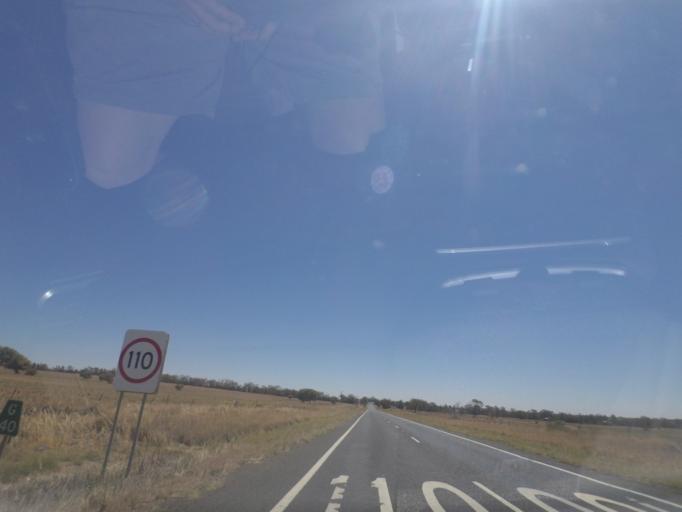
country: AU
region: New South Wales
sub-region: Gilgandra
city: Gilgandra
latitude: -31.4685
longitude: 148.9272
